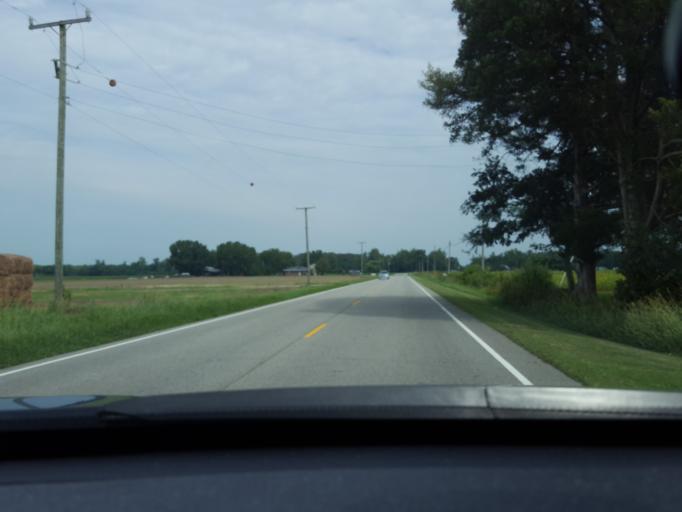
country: US
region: North Carolina
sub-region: Chowan County
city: Edenton
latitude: 36.1948
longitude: -76.6607
